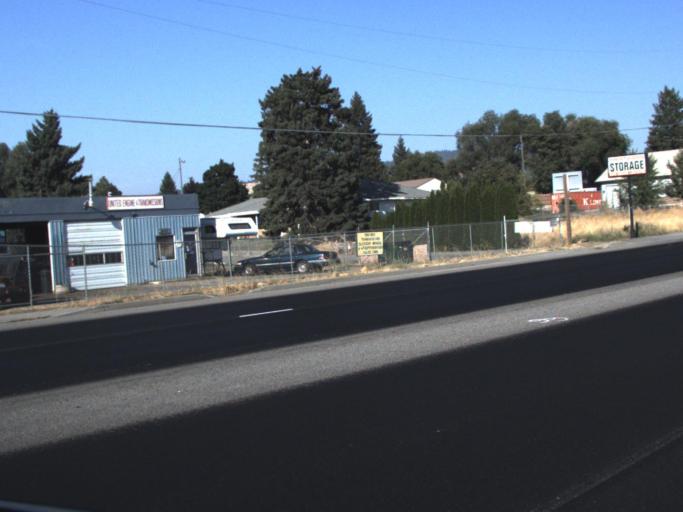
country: US
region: Washington
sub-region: Spokane County
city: Trentwood
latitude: 47.6940
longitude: -117.2278
